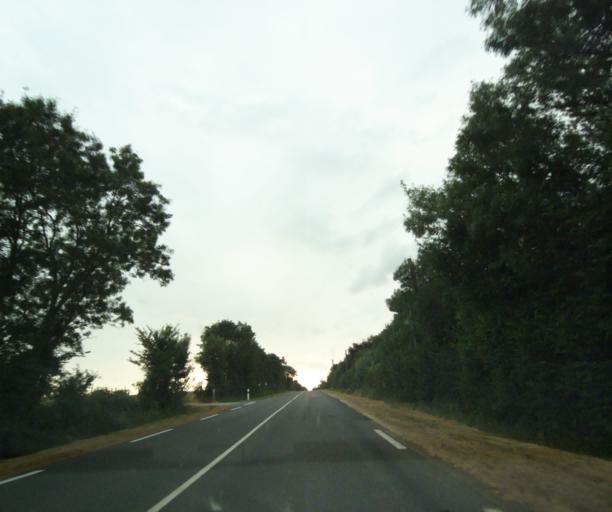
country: FR
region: Pays de la Loire
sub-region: Departement de la Vendee
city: Moutiers-les-Mauxfaits
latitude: 46.4550
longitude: -1.4234
